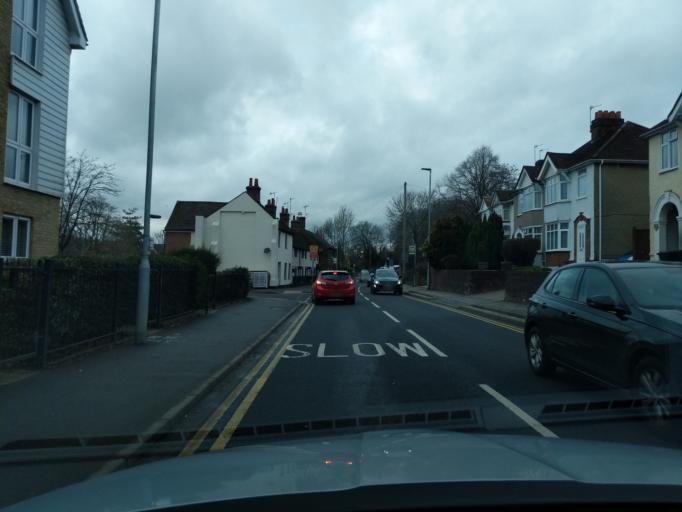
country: GB
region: England
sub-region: Hertfordshire
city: Kings Langley
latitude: 51.7304
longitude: -0.4514
